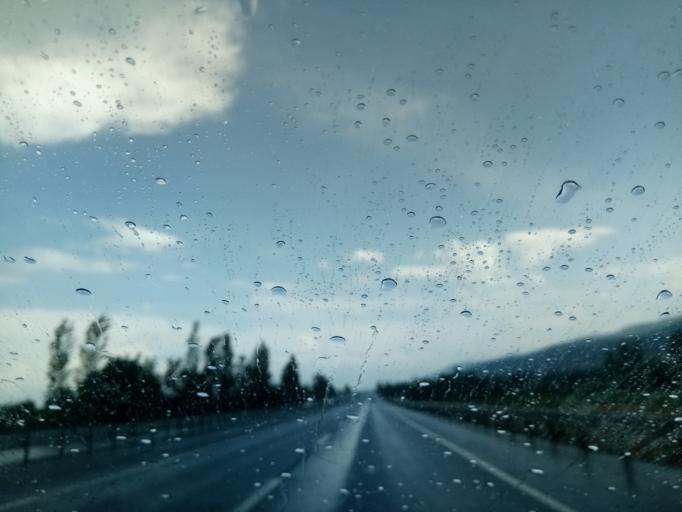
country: TR
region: Afyonkarahisar
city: Sultandagi
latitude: 38.4690
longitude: 31.2981
